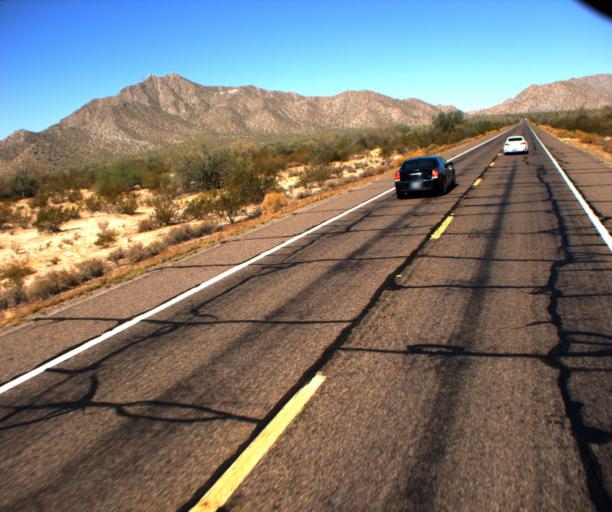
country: US
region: Arizona
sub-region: Pinal County
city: Blackwater
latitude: 33.0183
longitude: -111.6506
